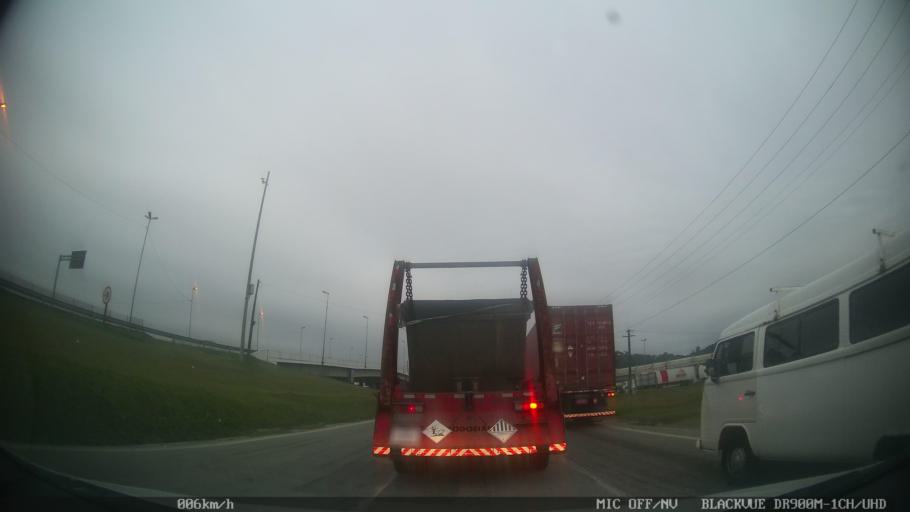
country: BR
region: Santa Catarina
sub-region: Itajai
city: Itajai
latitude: -26.8892
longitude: -48.7221
